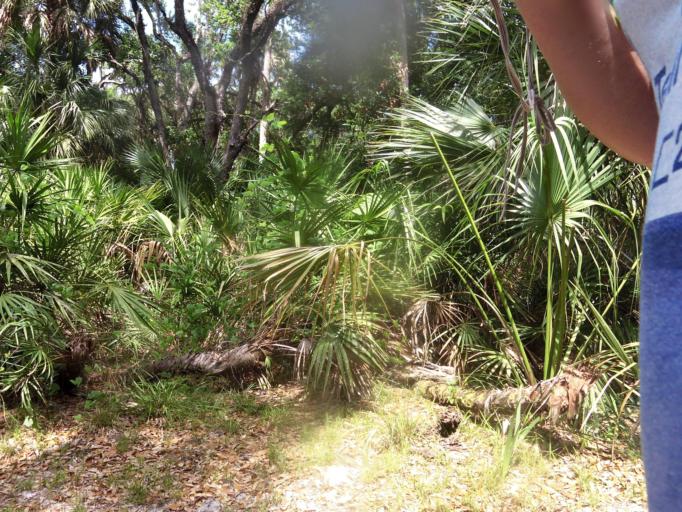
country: US
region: Florida
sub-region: Flagler County
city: Palm Coast
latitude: 29.6290
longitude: -81.2088
